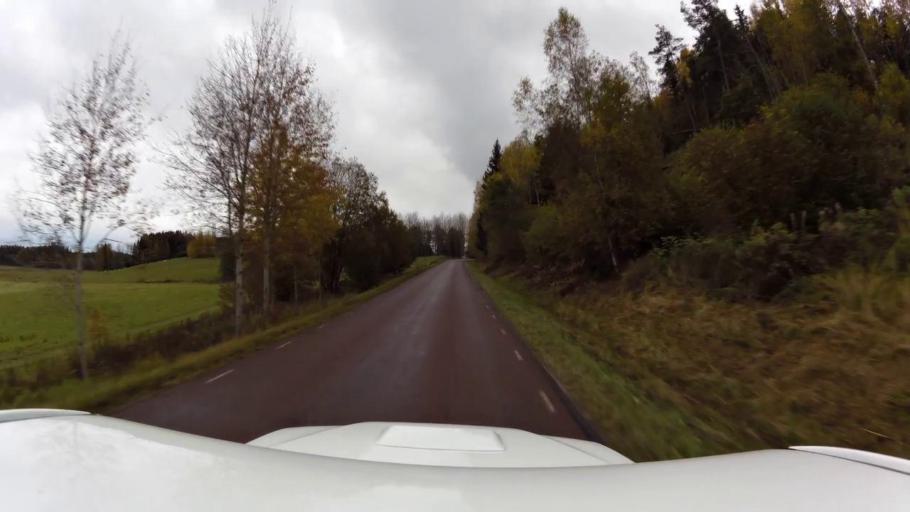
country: SE
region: OEstergoetland
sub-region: Linkopings Kommun
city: Ljungsbro
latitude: 58.5512
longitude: 15.5227
